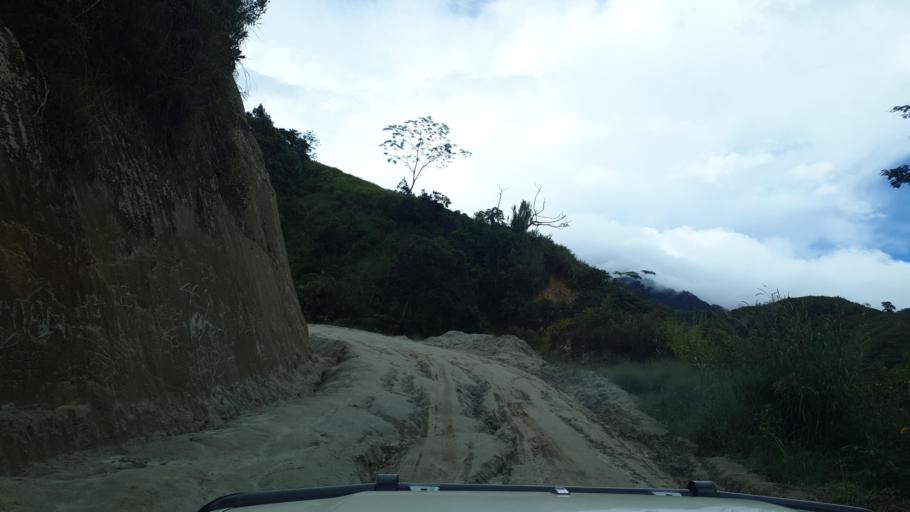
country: PG
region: Eastern Highlands
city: Goroka
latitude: -5.9255
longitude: 145.2627
